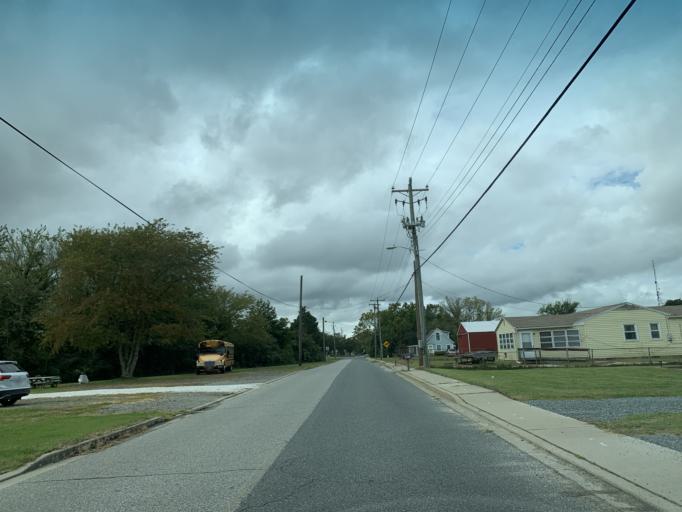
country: US
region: Maryland
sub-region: Caroline County
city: Denton
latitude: 38.8840
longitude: -75.8192
